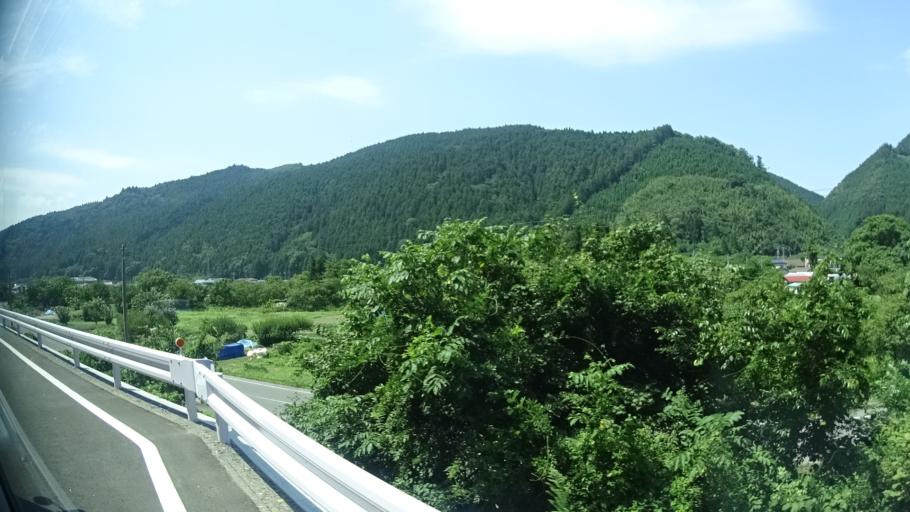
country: JP
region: Miyagi
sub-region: Oshika Gun
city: Onagawa Cho
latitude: 38.6327
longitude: 141.3613
